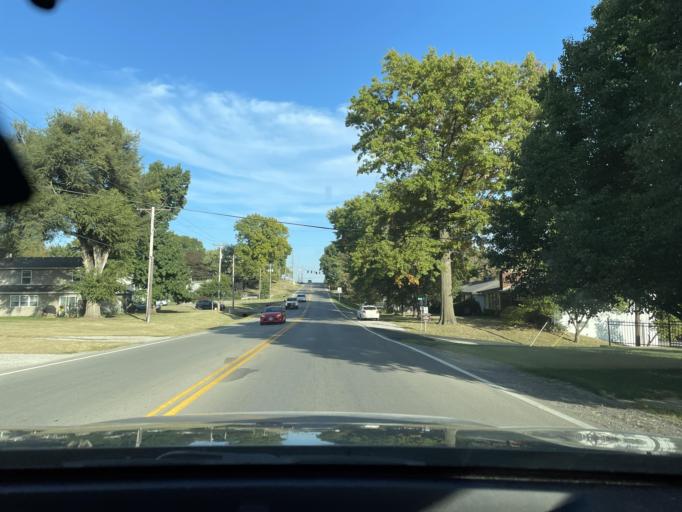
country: US
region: Missouri
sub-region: Buchanan County
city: Saint Joseph
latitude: 39.7552
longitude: -94.8001
